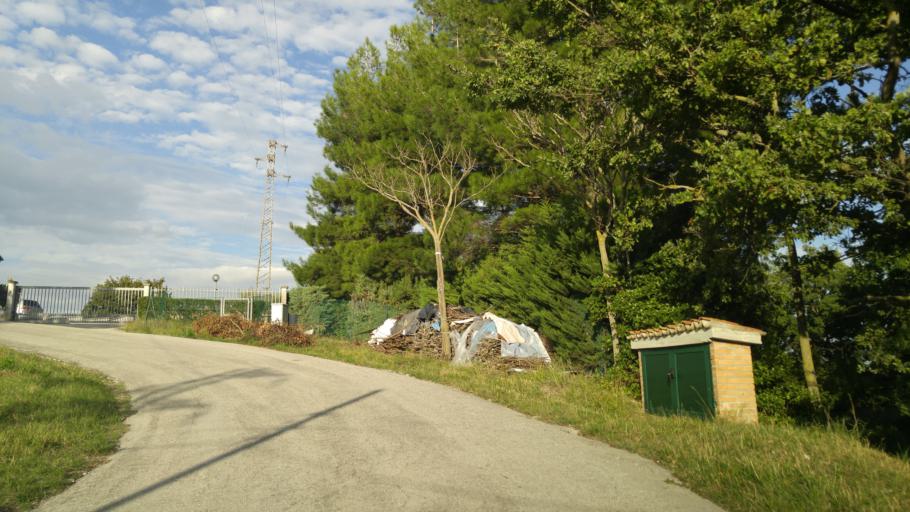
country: IT
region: The Marches
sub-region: Provincia di Pesaro e Urbino
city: Cagli
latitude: 43.5594
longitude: 12.6317
